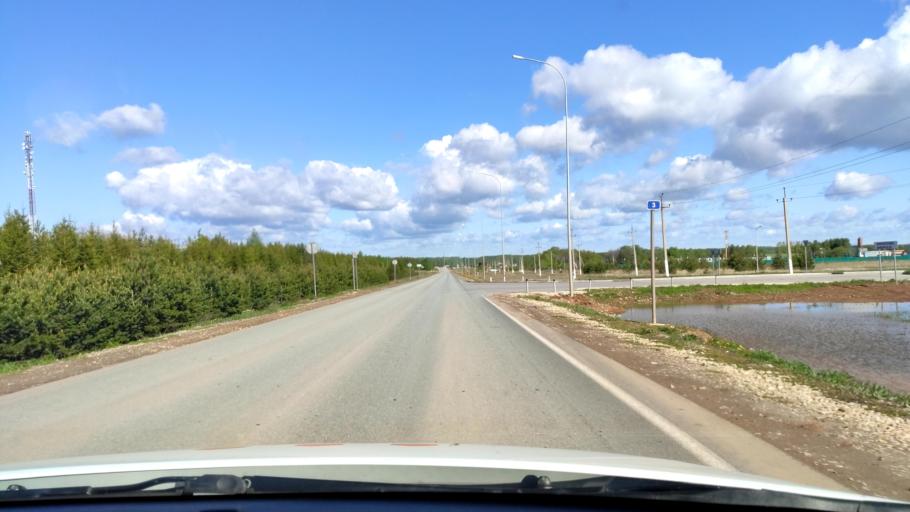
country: RU
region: Tatarstan
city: Sviyazhsk
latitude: 55.7422
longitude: 48.7312
